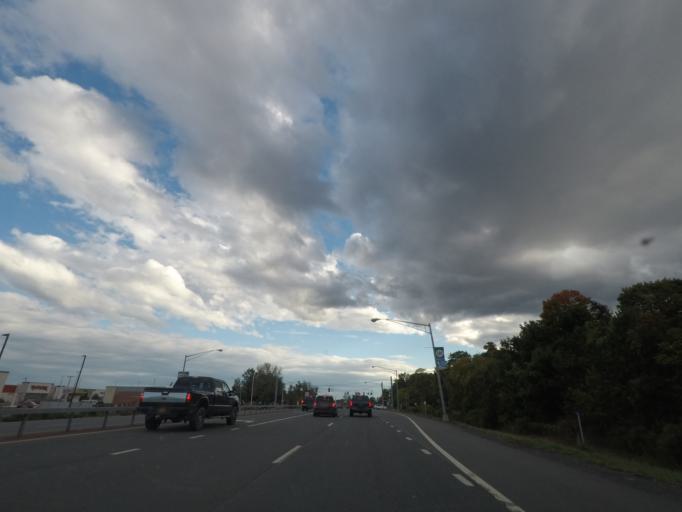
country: US
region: New York
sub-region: Albany County
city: McKownville
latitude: 42.6974
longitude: -73.8502
